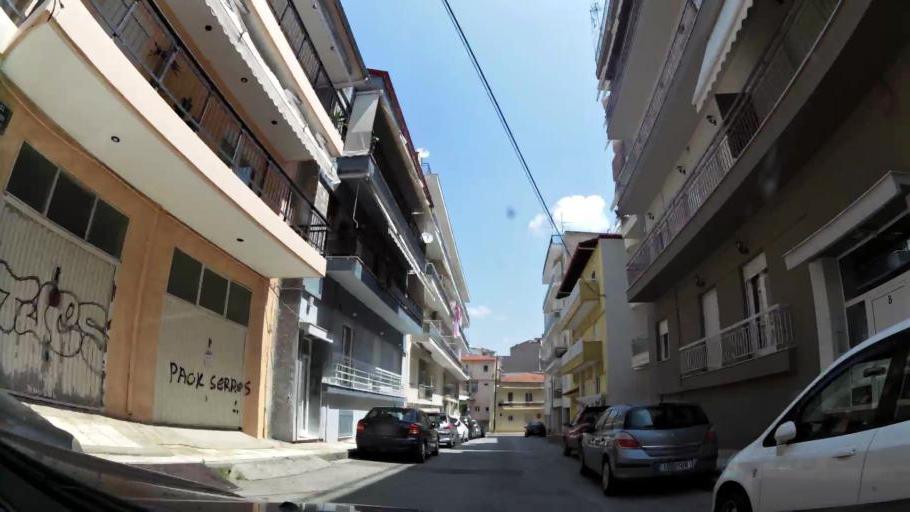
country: GR
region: West Macedonia
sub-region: Nomos Kozanis
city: Kozani
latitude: 40.2984
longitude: 21.7837
